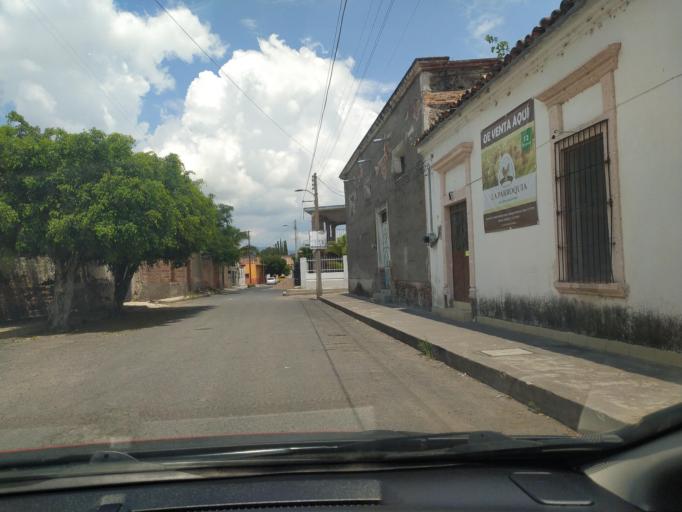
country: MX
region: Jalisco
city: Villa Corona
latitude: 20.3524
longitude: -103.6720
